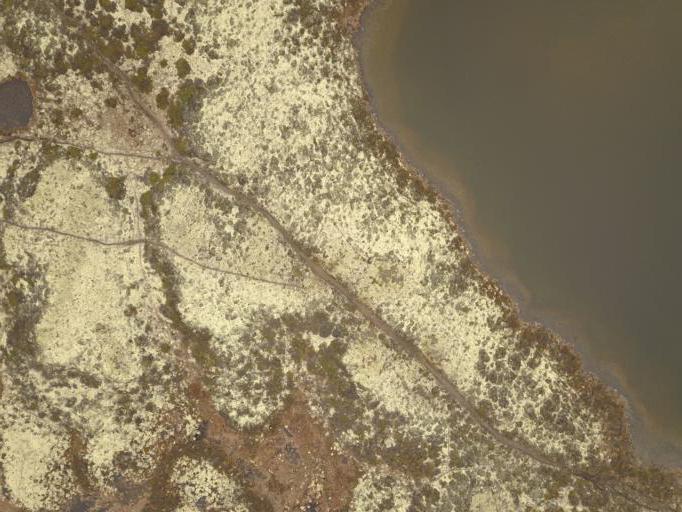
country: NO
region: Hedmark
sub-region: Folldal
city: Folldal
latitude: 62.2288
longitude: 9.6481
